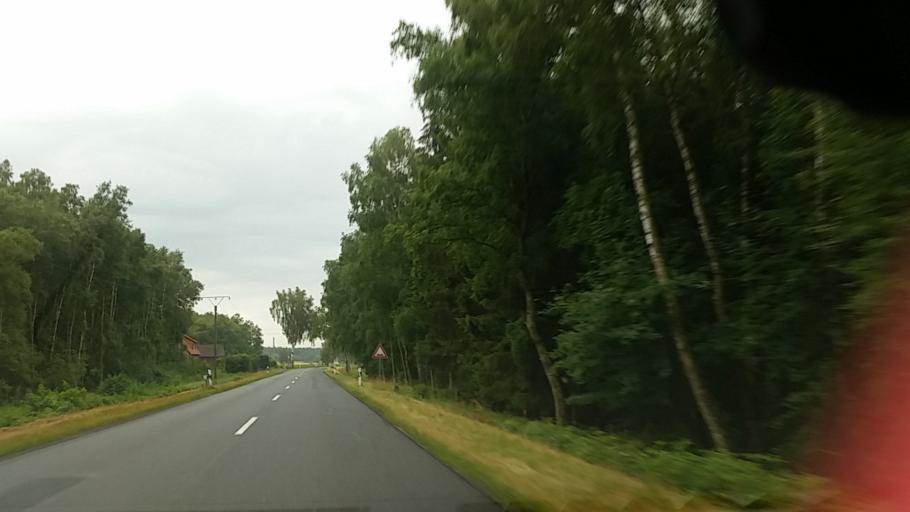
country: DE
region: Lower Saxony
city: Schoneworde
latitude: 52.6089
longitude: 10.6888
